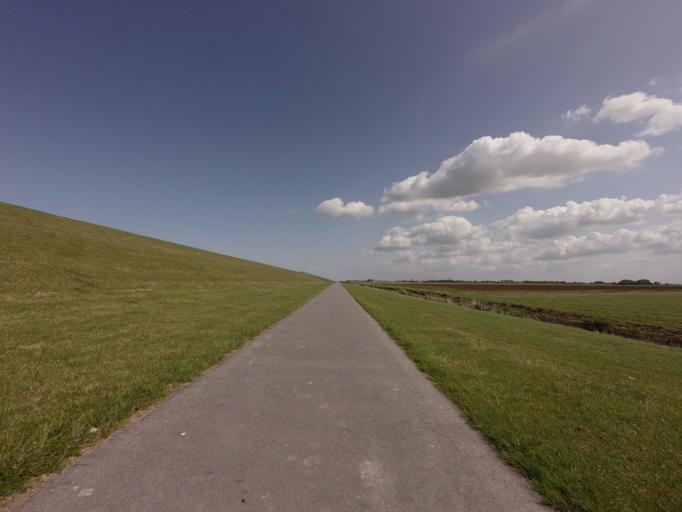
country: NL
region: Friesland
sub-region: Gemeente Dongeradeel
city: Holwerd
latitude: 53.3713
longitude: 5.8623
